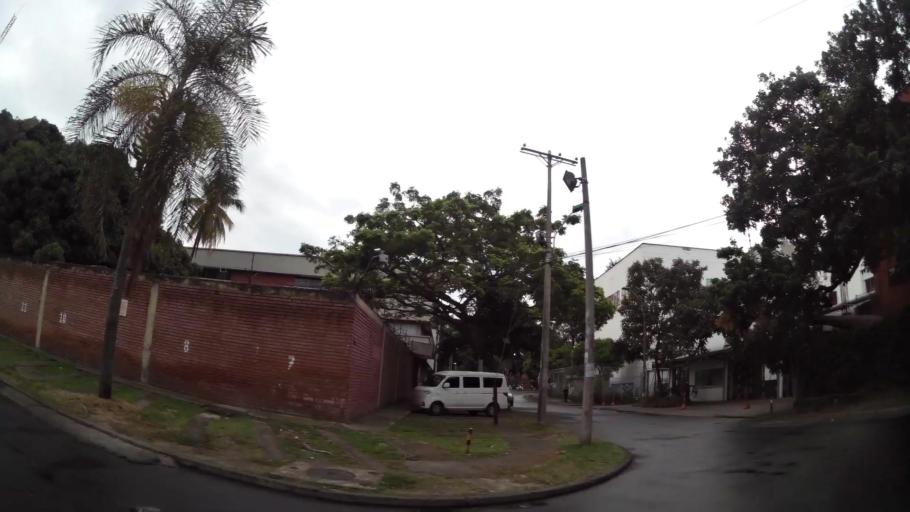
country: CO
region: Valle del Cauca
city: Cali
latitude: 3.4859
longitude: -76.5134
